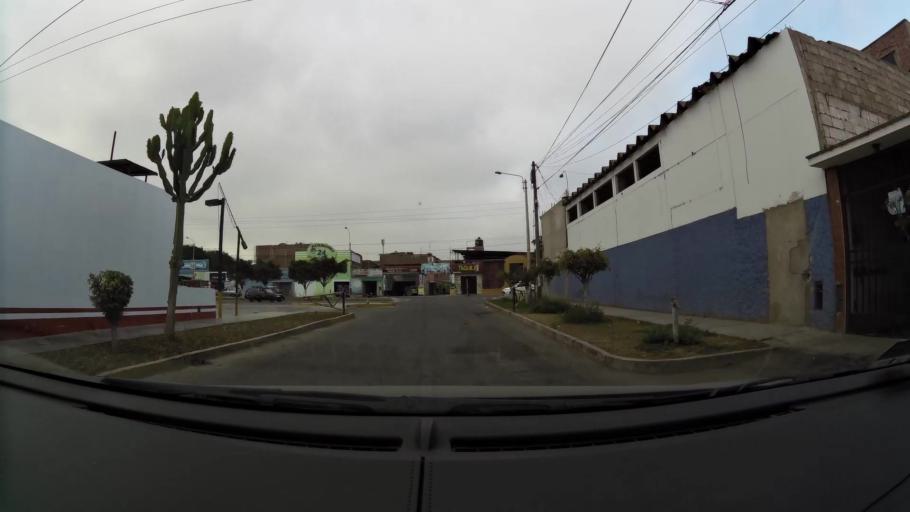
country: PE
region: La Libertad
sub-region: Provincia de Trujillo
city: Trujillo
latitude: -8.1015
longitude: -79.0263
